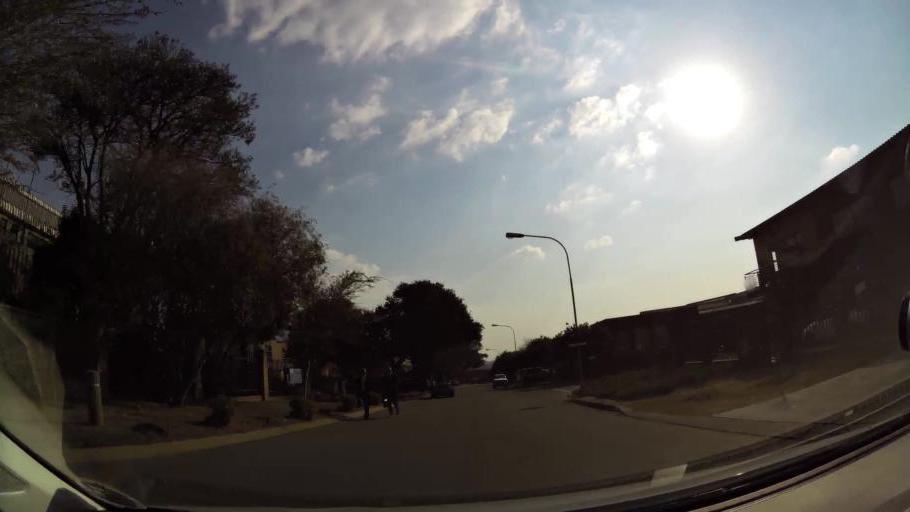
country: ZA
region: Gauteng
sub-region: City of Johannesburg Metropolitan Municipality
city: Modderfontein
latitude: -26.1072
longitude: 28.1743
